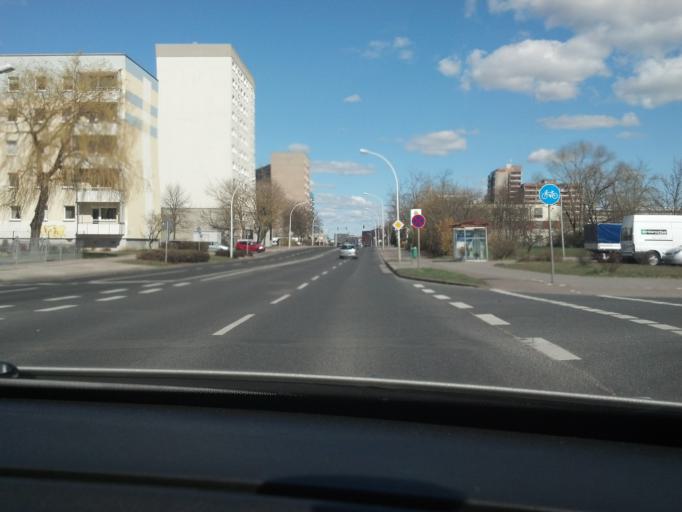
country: DE
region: Mecklenburg-Vorpommern
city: Neubrandenburg
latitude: 53.5508
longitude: 13.2925
